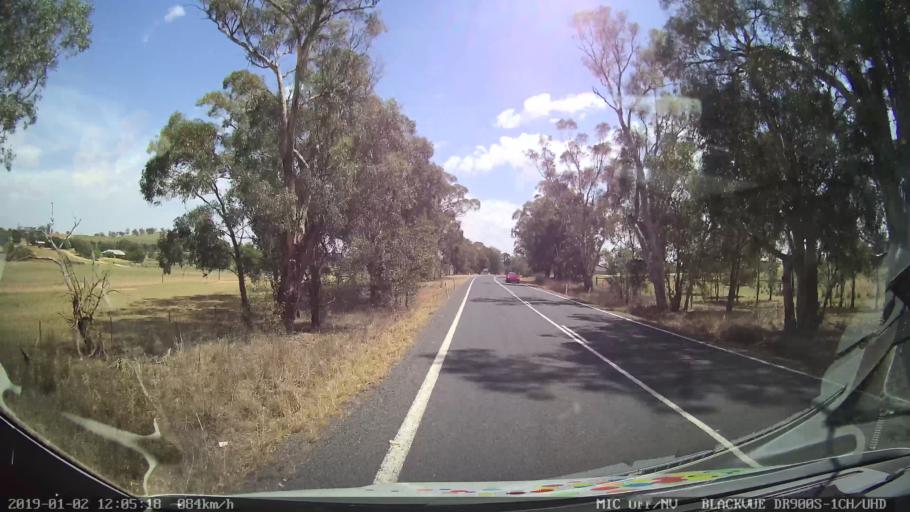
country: AU
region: New South Wales
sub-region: Young
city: Young
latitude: -34.5160
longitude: 148.3025
